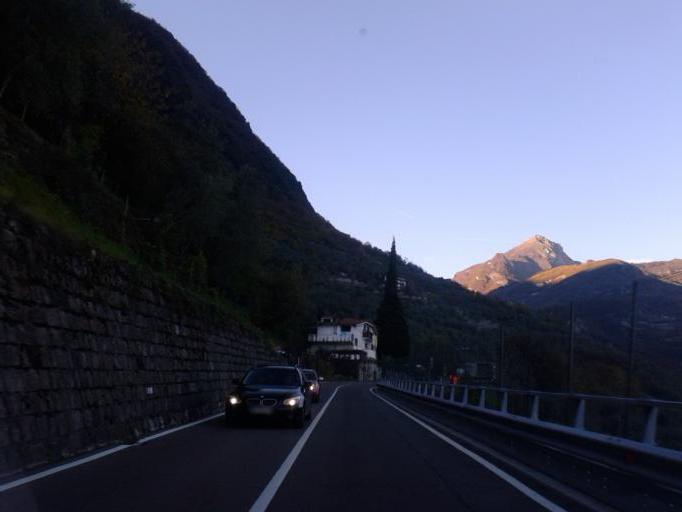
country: IT
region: Trentino-Alto Adige
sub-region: Provincia di Trento
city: Riva del Garda
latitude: 45.9009
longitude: 10.8344
